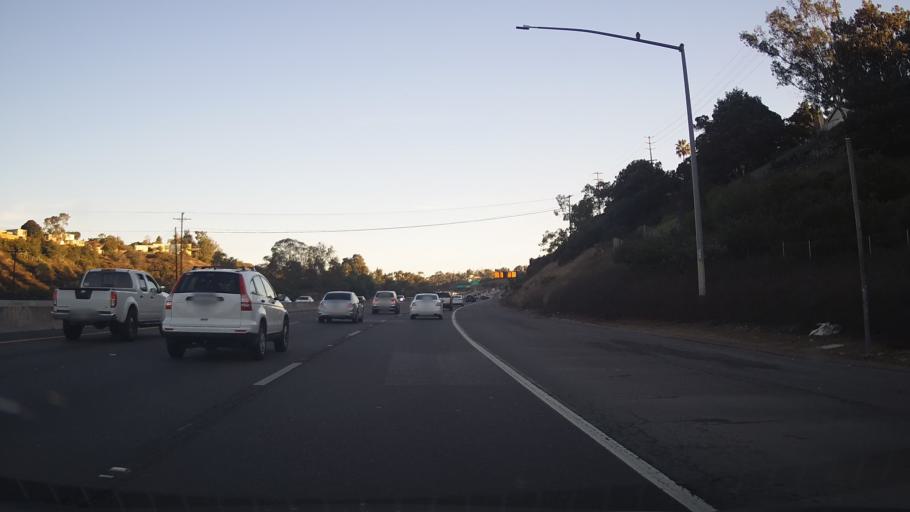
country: US
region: California
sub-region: San Diego County
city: San Diego
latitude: 32.7207
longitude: -117.1166
